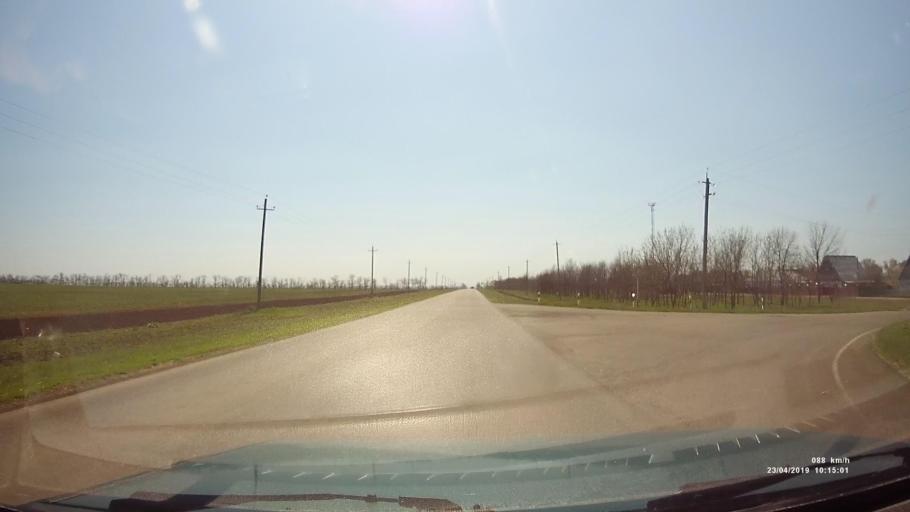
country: RU
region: Rostov
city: Sovetskoye
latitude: 46.6712
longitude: 42.3767
